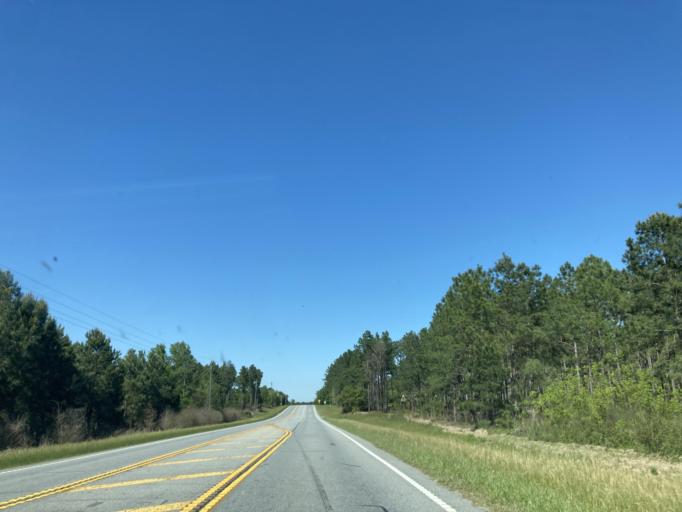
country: US
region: Georgia
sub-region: Baker County
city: Newton
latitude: 31.2400
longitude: -84.4346
